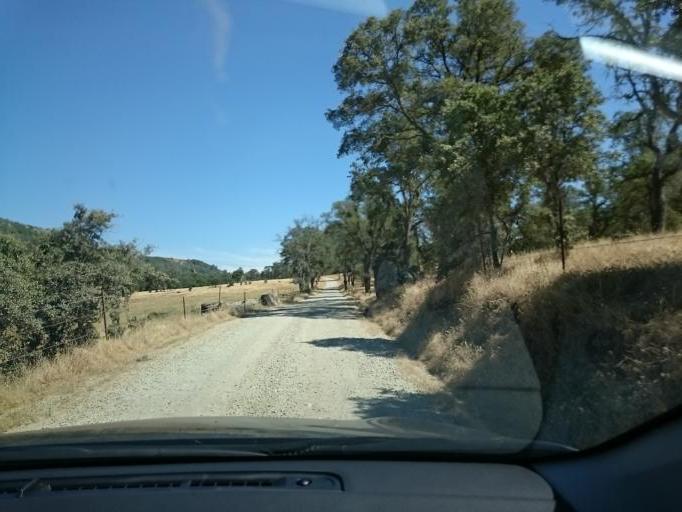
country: US
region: California
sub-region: Calaveras County
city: Rancho Calaveras
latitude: 38.1065
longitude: -120.7692
